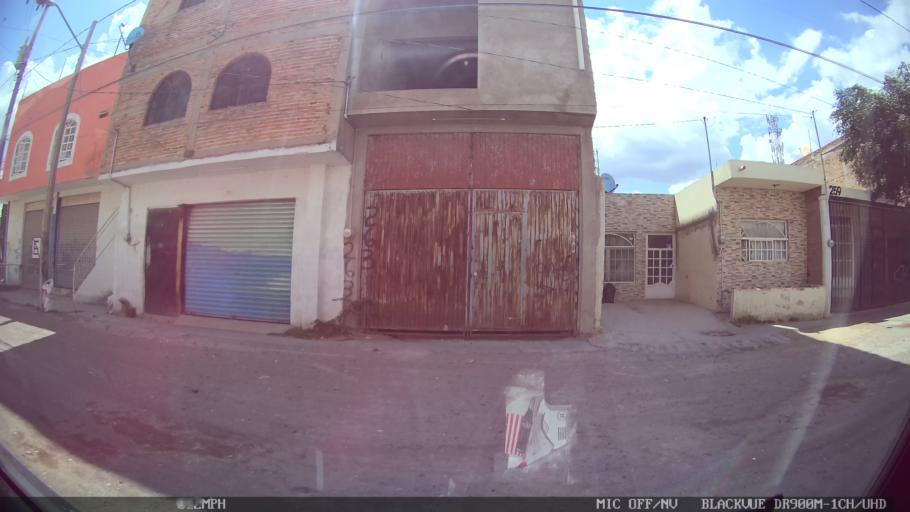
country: MX
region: Jalisco
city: Tlaquepaque
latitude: 20.6683
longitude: -103.2560
